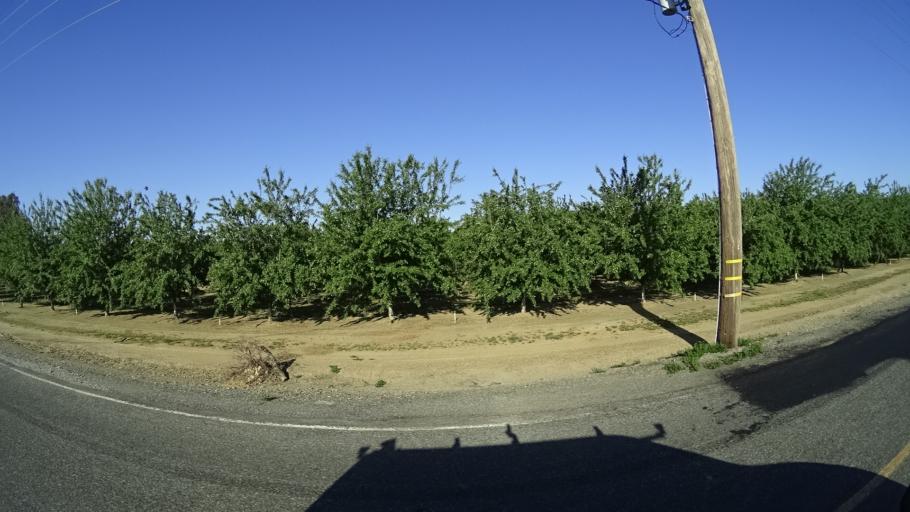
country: US
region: California
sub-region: Glenn County
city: Orland
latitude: 39.6986
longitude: -122.1779
